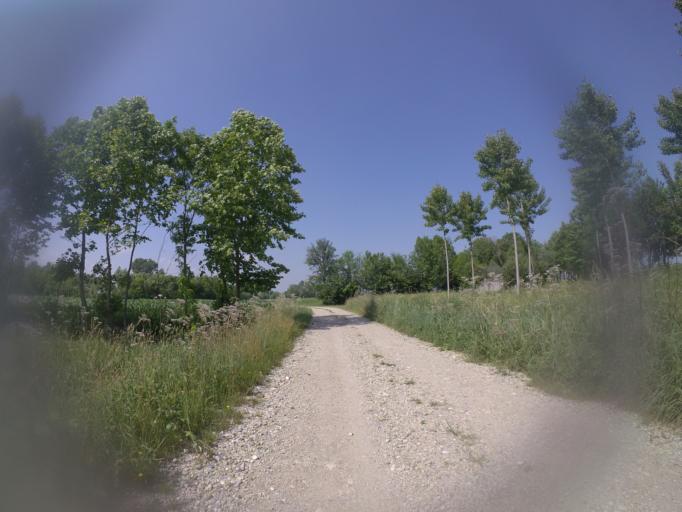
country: IT
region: Friuli Venezia Giulia
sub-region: Provincia di Udine
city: Bertiolo
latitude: 45.9367
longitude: 13.0273
